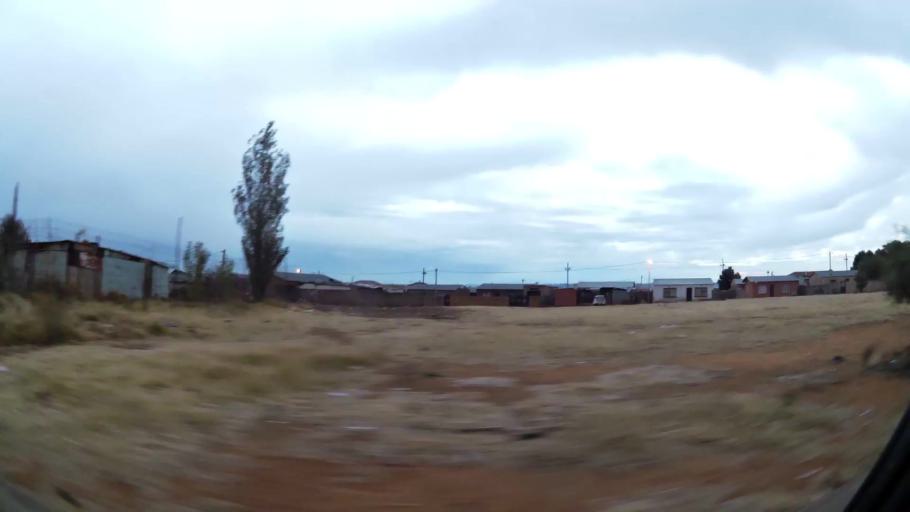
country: ZA
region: Gauteng
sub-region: West Rand District Municipality
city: Randfontein
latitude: -26.1769
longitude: 27.7866
